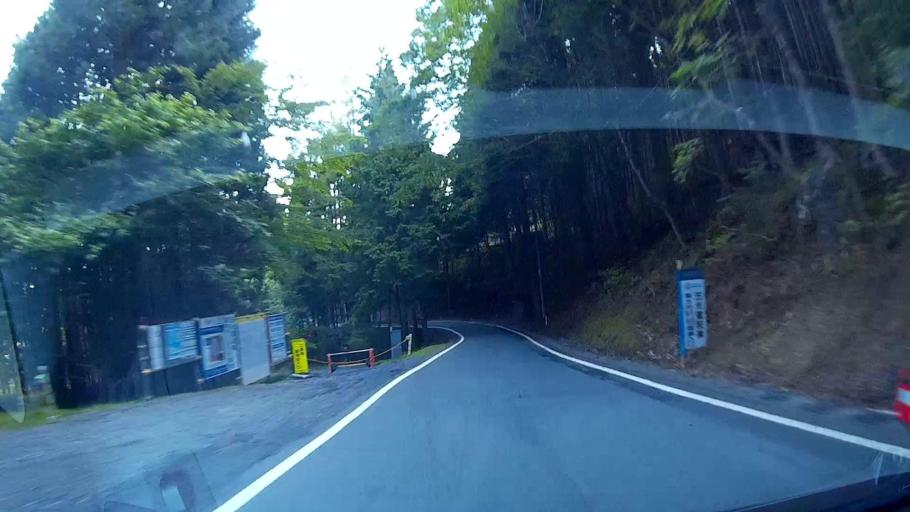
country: JP
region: Shizuoka
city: Shizuoka-shi
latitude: 35.1830
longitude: 138.2493
